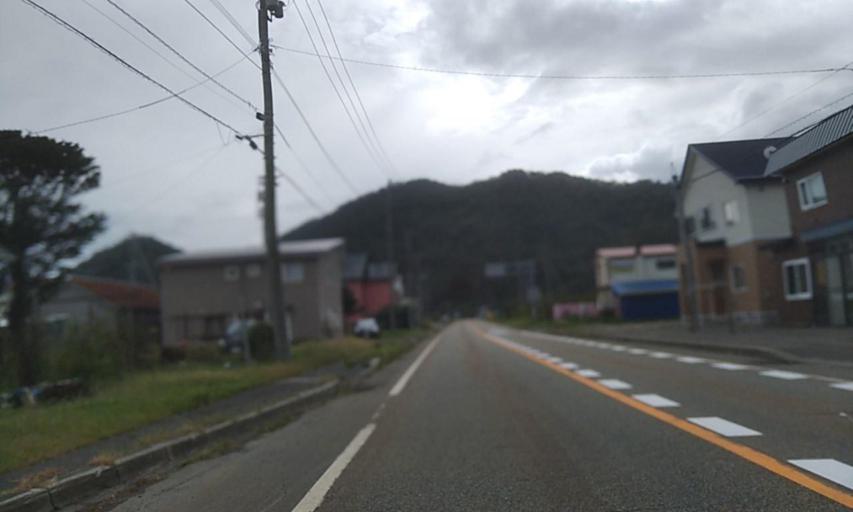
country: JP
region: Hokkaido
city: Obihiro
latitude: 42.1268
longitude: 143.3172
